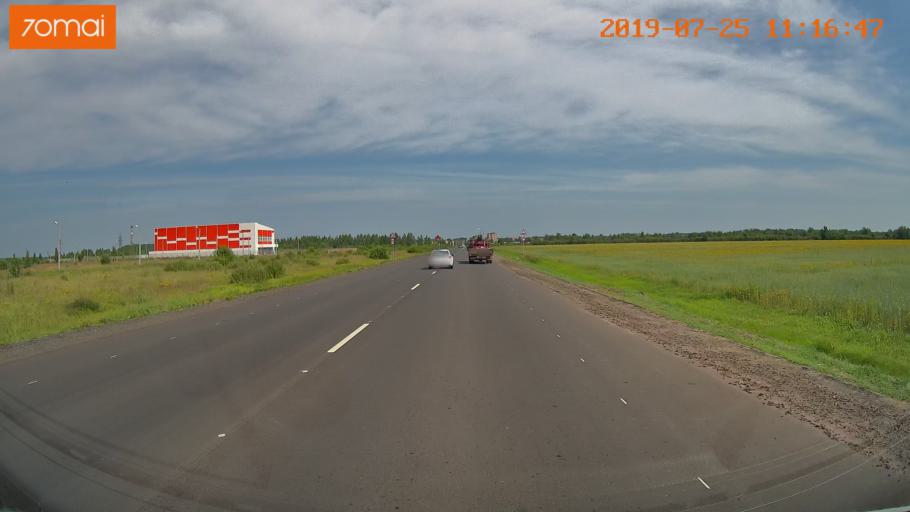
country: RU
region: Ivanovo
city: Privolzhsk
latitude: 57.3619
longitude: 41.2668
